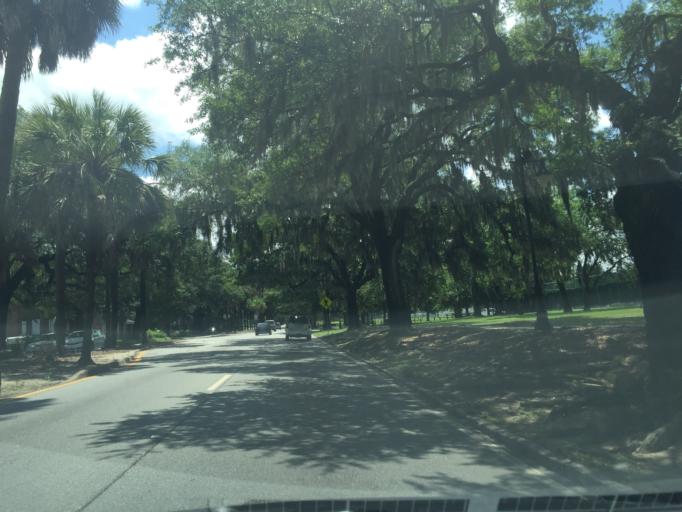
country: US
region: Georgia
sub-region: Chatham County
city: Thunderbolt
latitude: 32.0474
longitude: -81.0825
